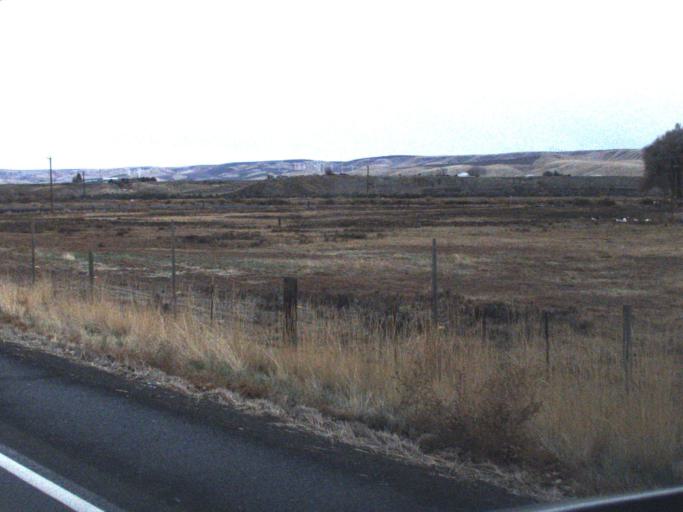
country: US
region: Washington
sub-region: Walla Walla County
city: Garrett
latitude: 46.0432
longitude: -118.6907
